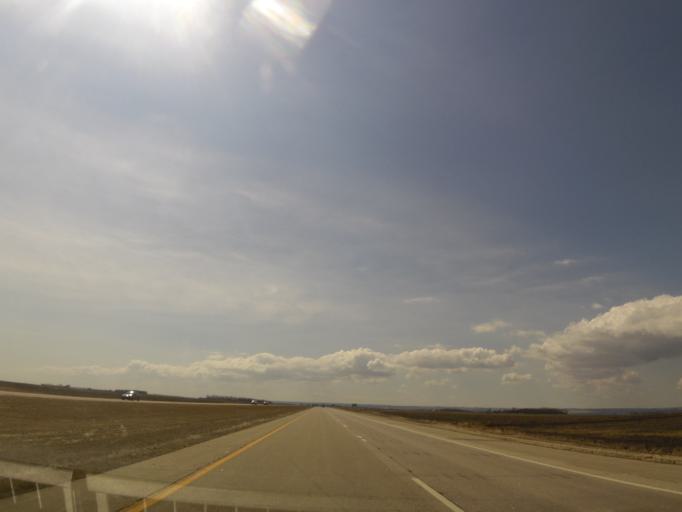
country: US
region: South Dakota
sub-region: Roberts County
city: Sisseton
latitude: 45.7224
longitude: -96.9480
